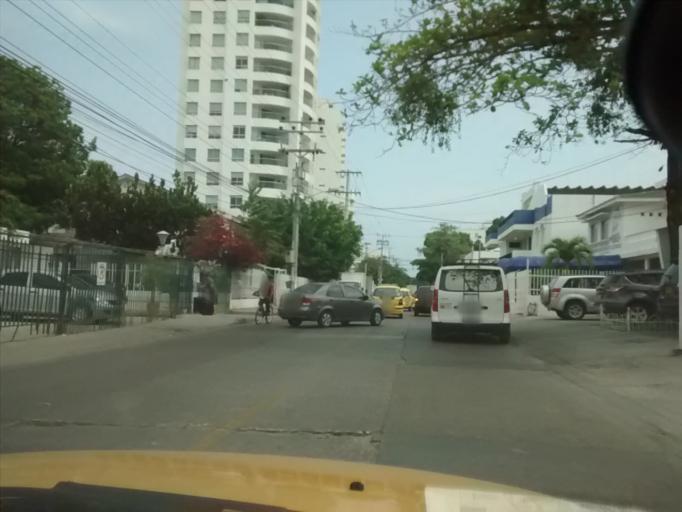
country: CO
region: Bolivar
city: Cartagena
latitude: 10.4131
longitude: -75.5372
